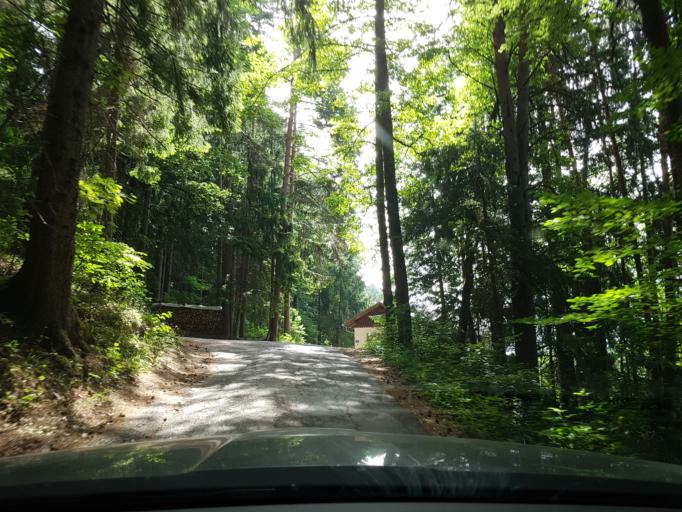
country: AT
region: Carinthia
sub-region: Politischer Bezirk Spittal an der Drau
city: Millstatt
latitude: 46.7763
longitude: 13.5584
